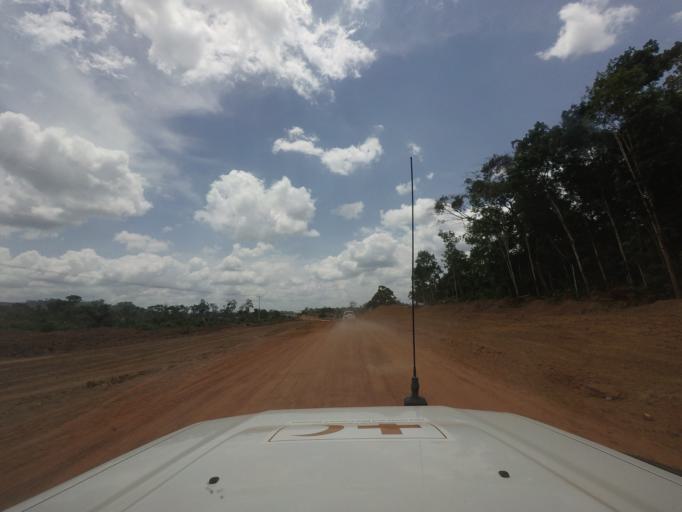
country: LR
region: Nimba
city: Sanniquellie
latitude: 7.2452
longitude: -8.8675
